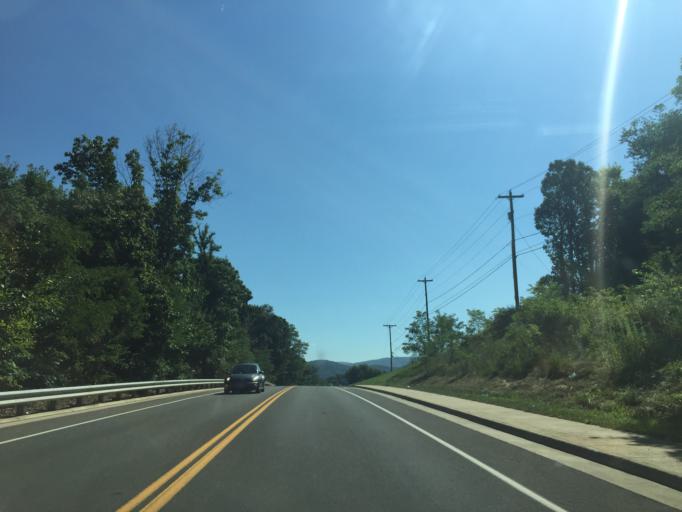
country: US
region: Virginia
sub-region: Warren County
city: Front Royal
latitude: 38.9294
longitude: -78.1650
